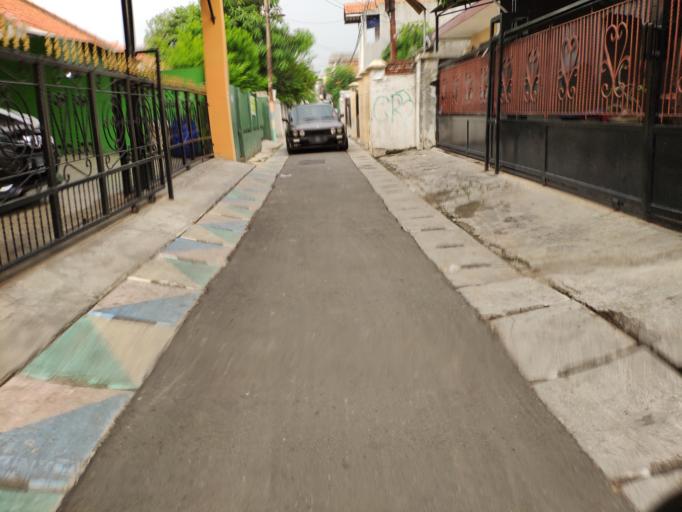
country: ID
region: Jakarta Raya
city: Jakarta
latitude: -6.1974
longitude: 106.8657
